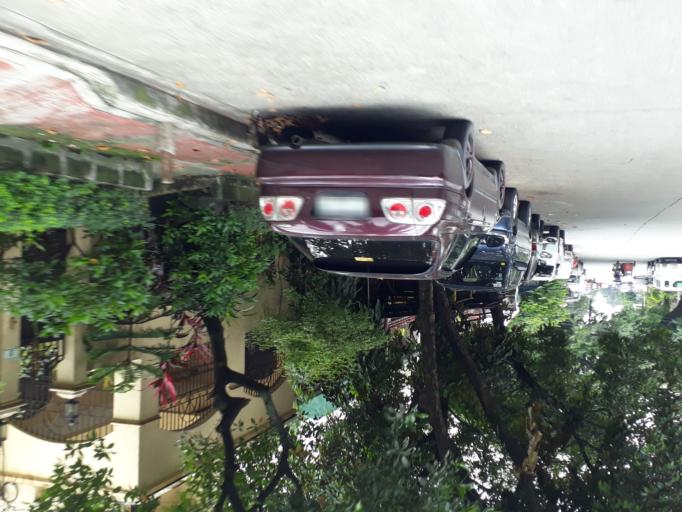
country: PH
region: Calabarzon
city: Bagong Pagasa
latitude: 14.6640
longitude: 121.0318
